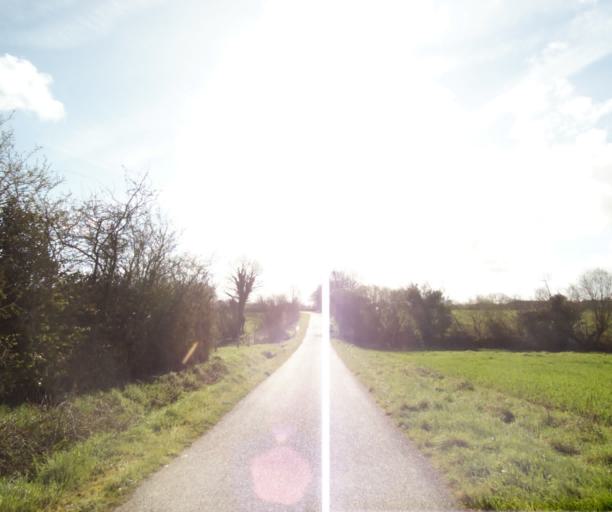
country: FR
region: Pays de la Loire
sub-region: Departement de la Loire-Atlantique
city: Bouvron
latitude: 47.4003
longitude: -1.8348
